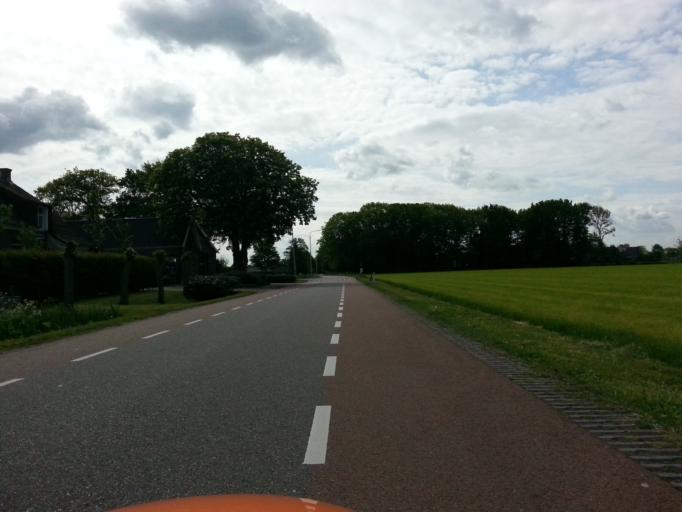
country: NL
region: Gelderland
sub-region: Gemeente Barneveld
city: Barneveld
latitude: 52.1065
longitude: 5.5608
